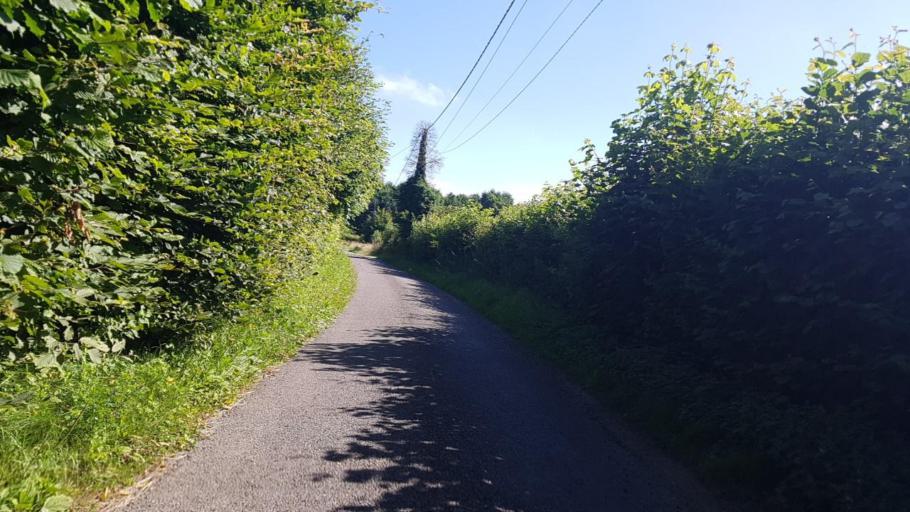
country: FR
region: Nord-Pas-de-Calais
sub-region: Departement du Nord
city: Anor
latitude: 49.9963
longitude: 4.1347
